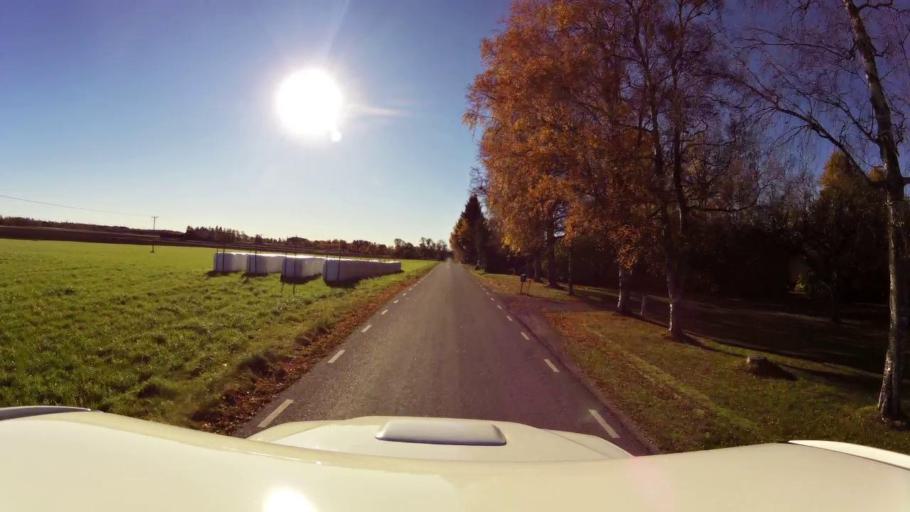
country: SE
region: OEstergoetland
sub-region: Linkopings Kommun
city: Ljungsbro
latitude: 58.5007
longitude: 15.4186
